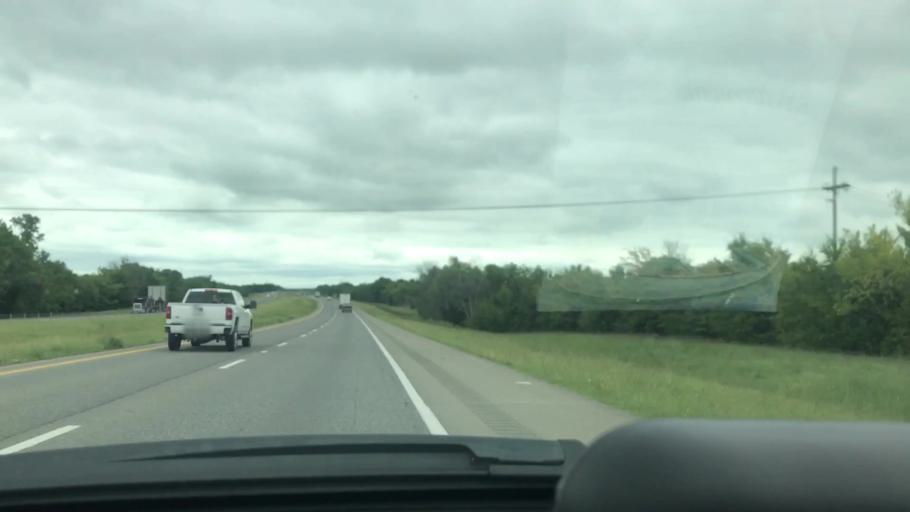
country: US
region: Oklahoma
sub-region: McIntosh County
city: Eufaula
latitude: 35.3766
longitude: -95.5693
